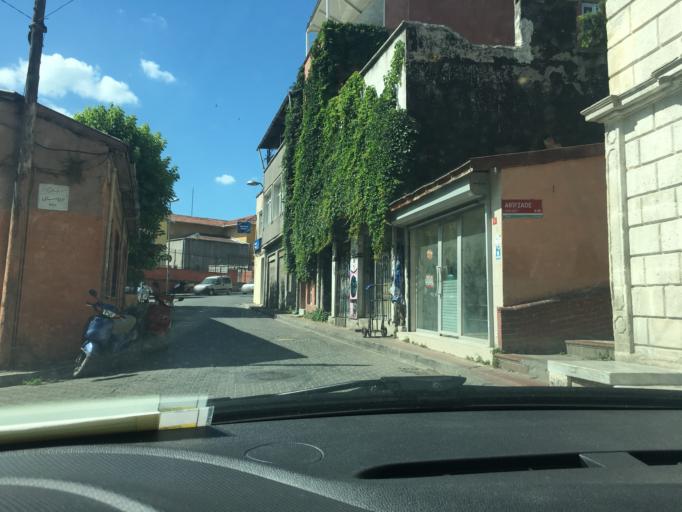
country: TR
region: Istanbul
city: Istanbul
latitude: 41.0193
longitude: 28.9549
